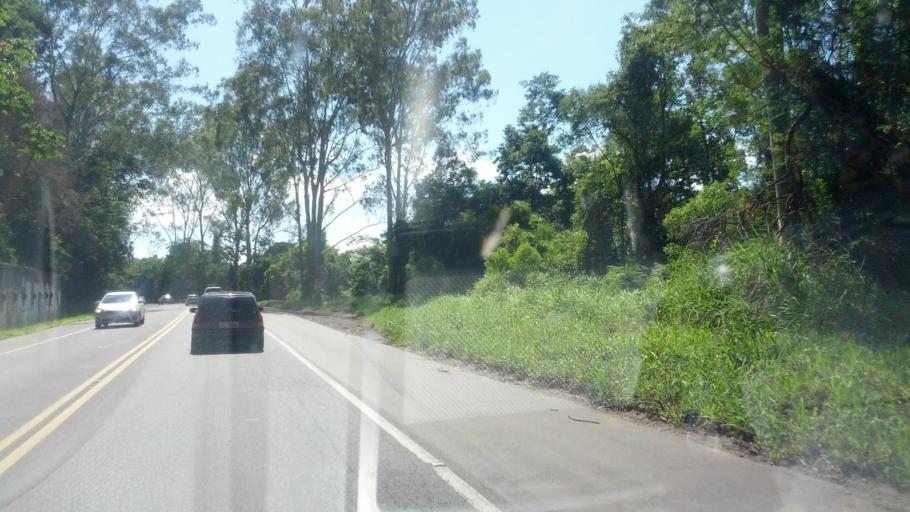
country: BR
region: Santa Catarina
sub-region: Ibirama
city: Ibirama
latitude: -27.1471
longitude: -49.5529
